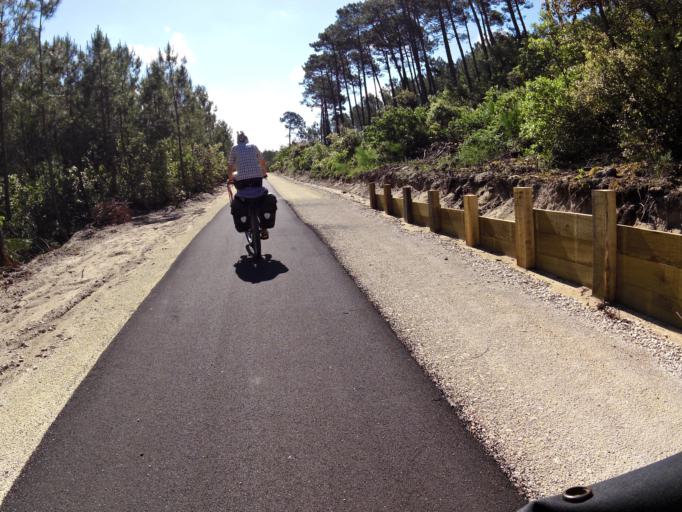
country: FR
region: Aquitaine
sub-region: Departement de la Gironde
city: Lacanau
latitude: 45.0292
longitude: -1.1726
